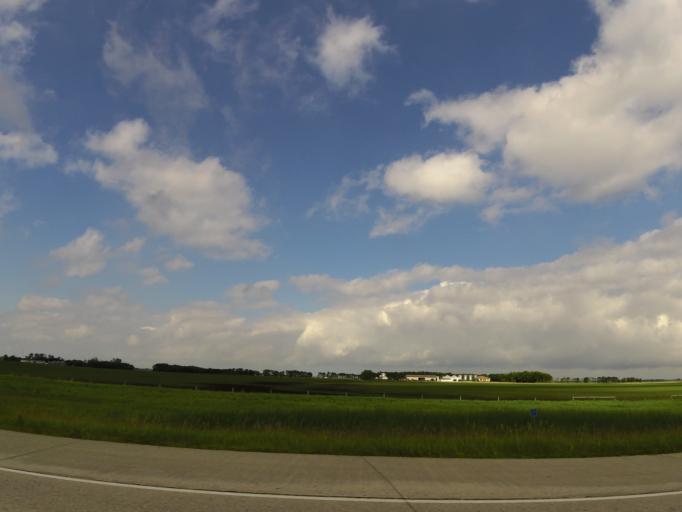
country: US
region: North Dakota
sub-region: Walsh County
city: Grafton
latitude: 48.3200
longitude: -97.1897
